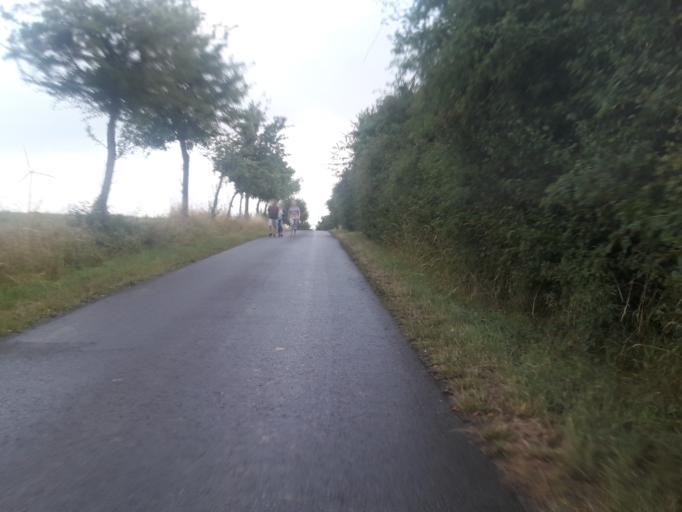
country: DE
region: North Rhine-Westphalia
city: Bad Lippspringe
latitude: 51.7349
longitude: 8.8224
